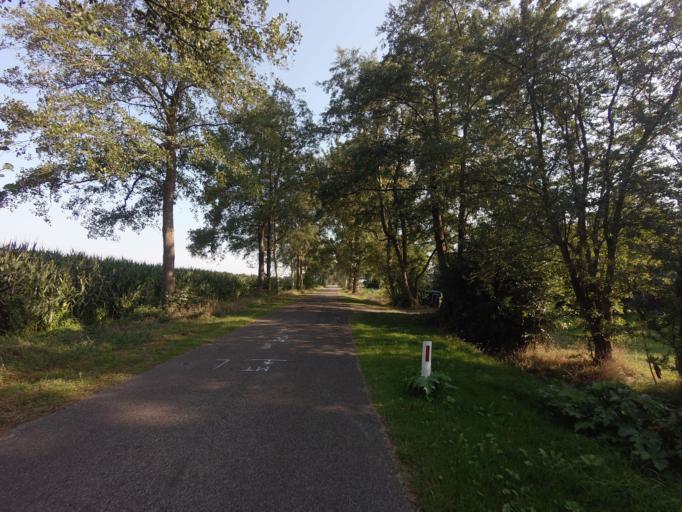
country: NL
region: Drenthe
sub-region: Gemeente Tynaarlo
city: Vries
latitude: 53.1290
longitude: 6.4909
